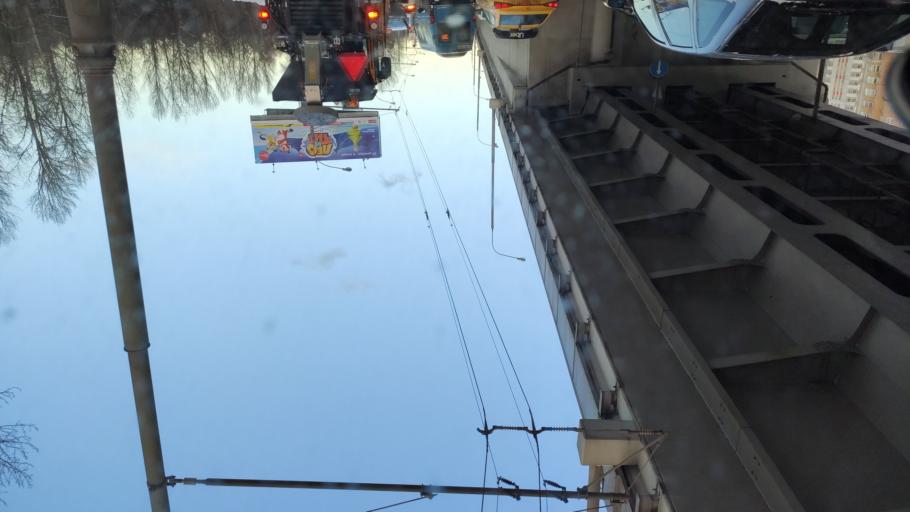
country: RU
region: Moscow
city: Orekhovo-Borisovo Severnoye
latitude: 55.6056
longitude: 37.6686
